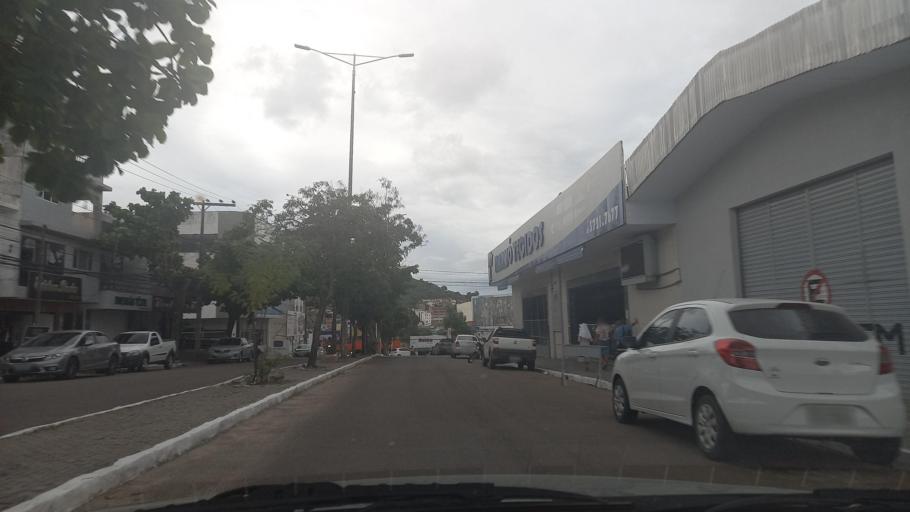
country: BR
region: Pernambuco
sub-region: Caruaru
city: Caruaru
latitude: -8.2946
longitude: -35.9742
